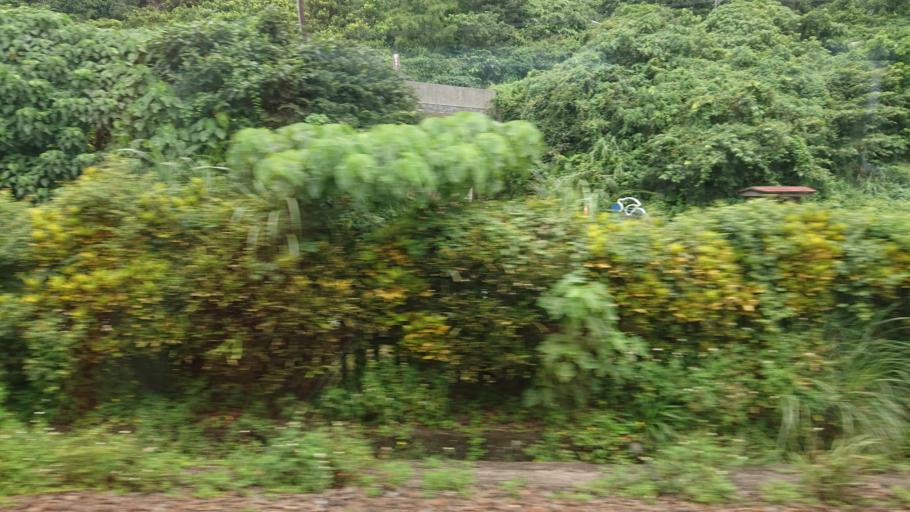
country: TW
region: Taiwan
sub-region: Keelung
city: Keelung
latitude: 24.9814
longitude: 121.9526
